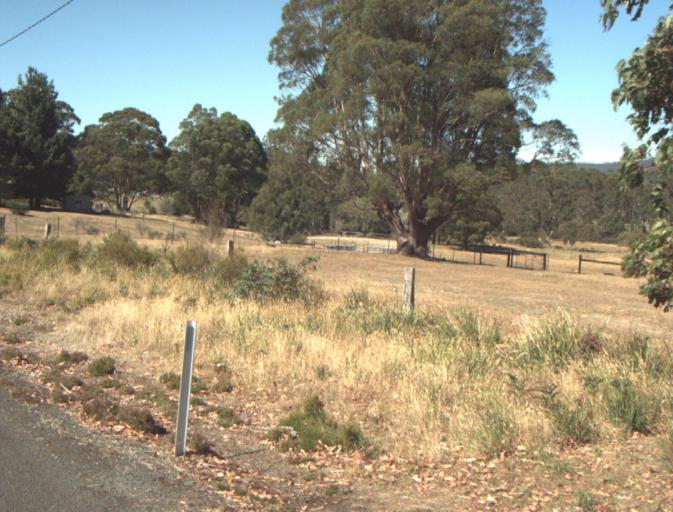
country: AU
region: Tasmania
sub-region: Launceston
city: Newstead
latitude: -41.3072
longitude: 147.3184
